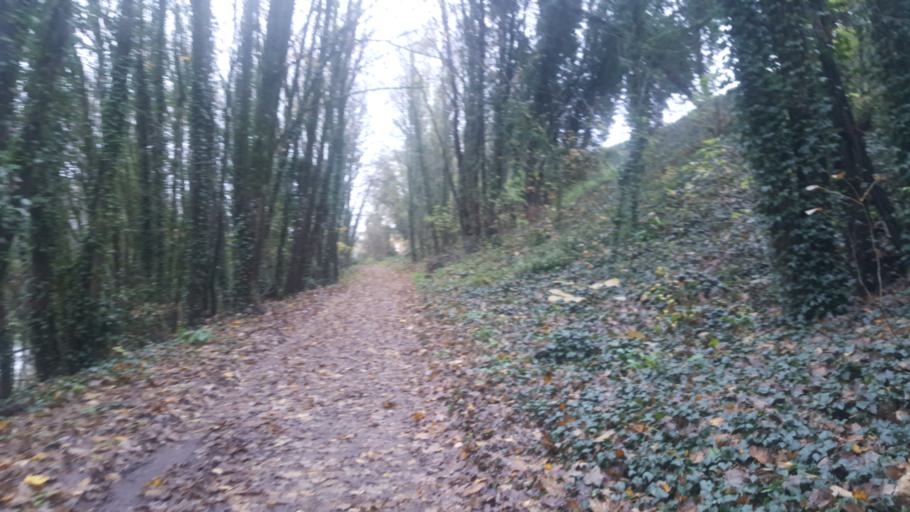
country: FR
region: Poitou-Charentes
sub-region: Departement des Deux-Sevres
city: Melle
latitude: 46.2265
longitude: -0.1493
